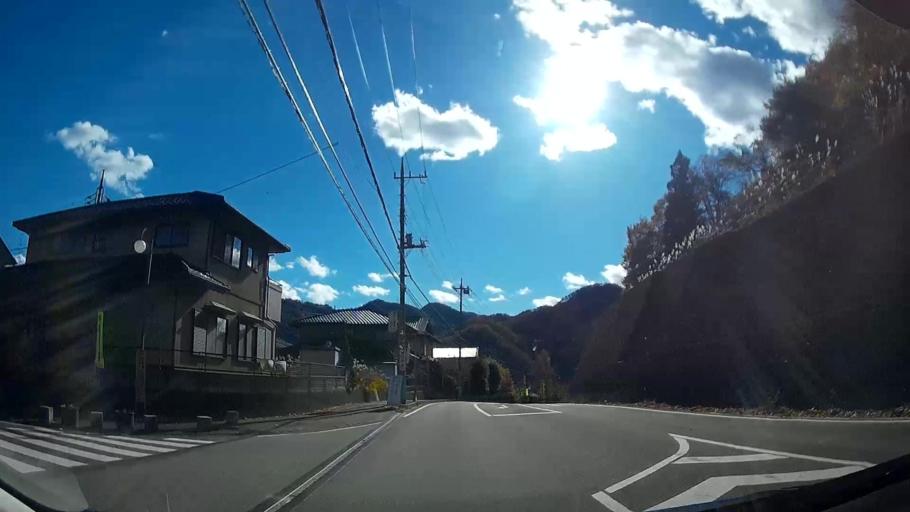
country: JP
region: Yamanashi
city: Otsuki
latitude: 35.6191
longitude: 138.9542
